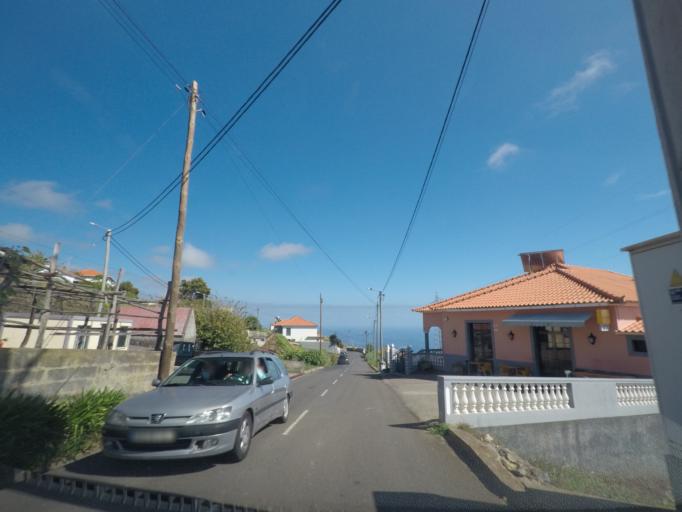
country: PT
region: Madeira
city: Ponta do Sol
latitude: 32.6976
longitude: -17.1054
